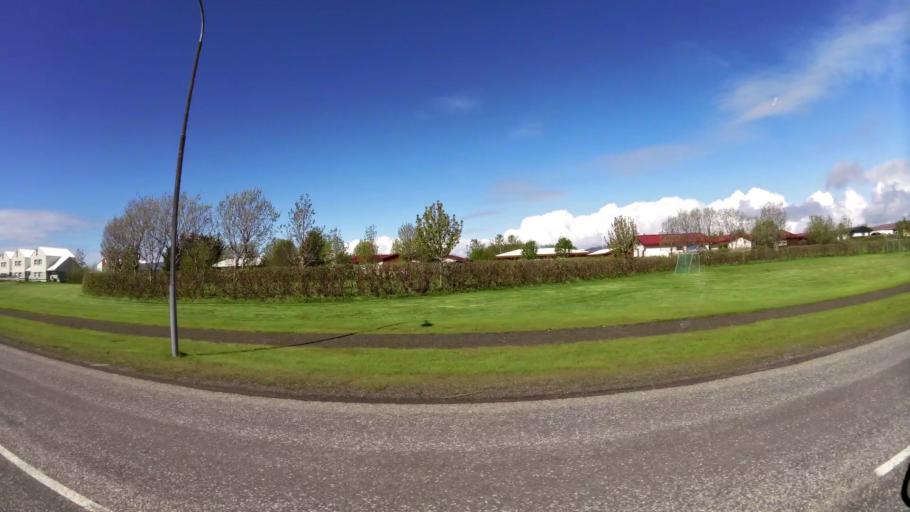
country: IS
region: East
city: Hoefn
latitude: 64.2616
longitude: -15.2031
